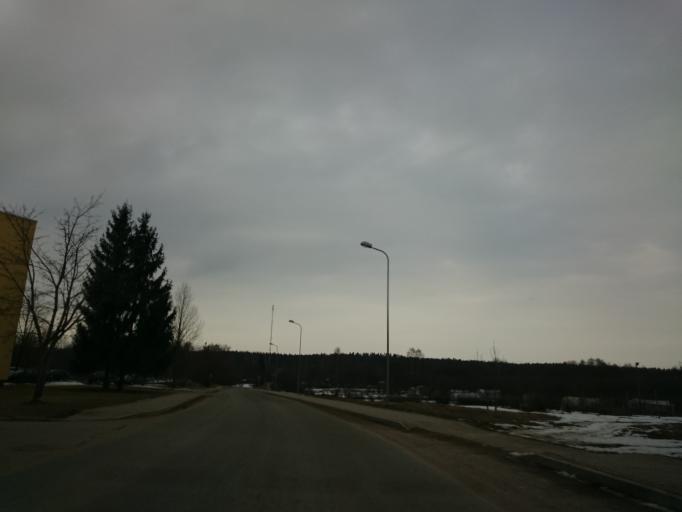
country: LV
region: Cesu Rajons
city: Cesis
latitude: 57.3177
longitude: 25.2591
